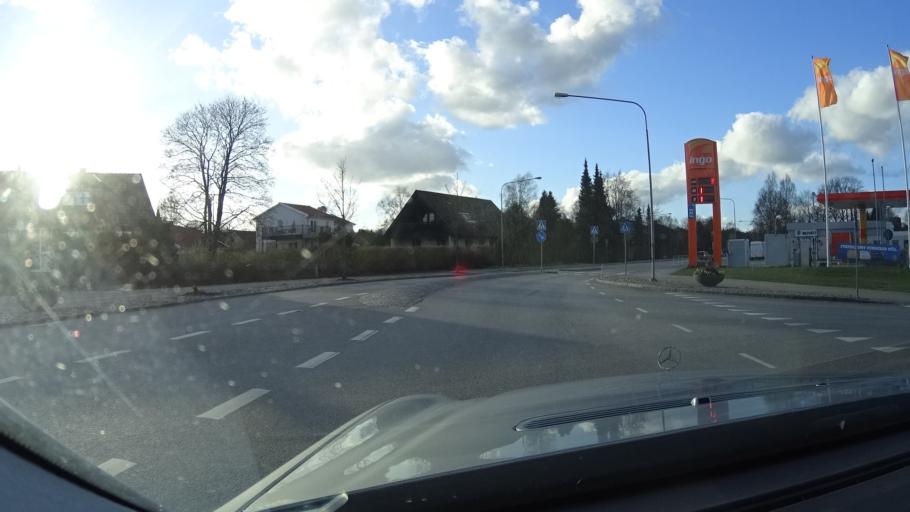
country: SE
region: Skane
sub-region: Hoors Kommun
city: Hoeoer
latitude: 55.9268
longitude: 13.5448
